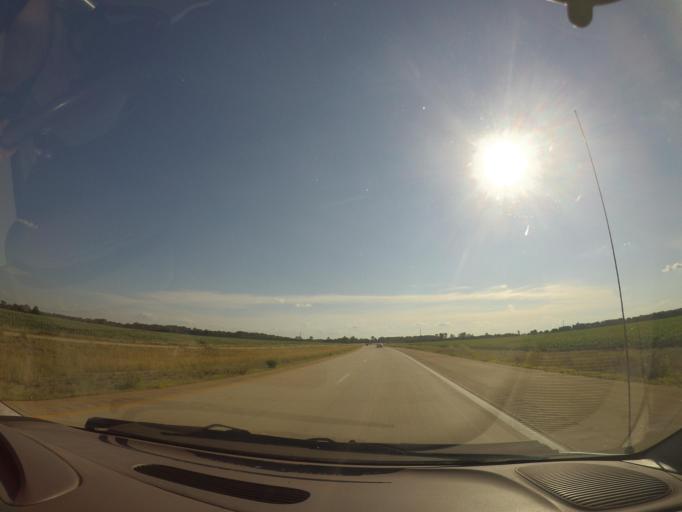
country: US
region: Ohio
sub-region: Lucas County
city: Whitehouse
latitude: 41.4329
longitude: -83.8808
